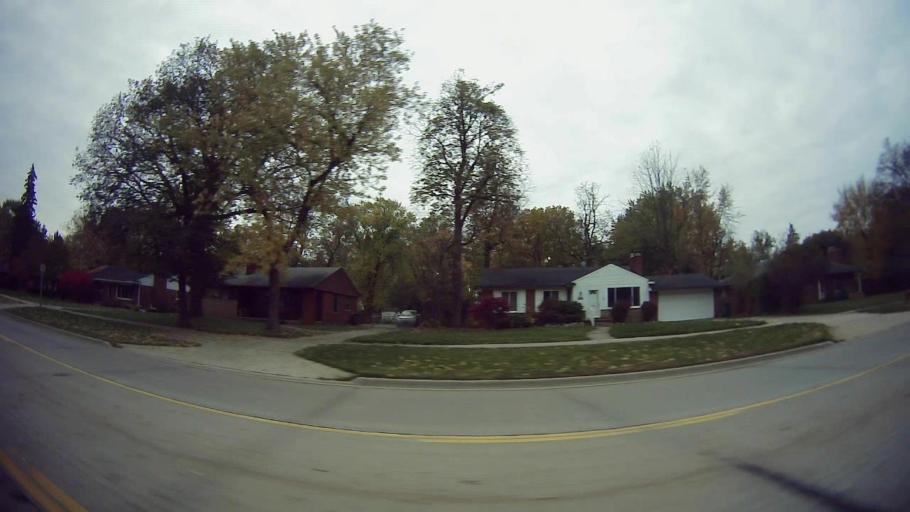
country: US
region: Michigan
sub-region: Oakland County
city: Beverly Hills
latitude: 42.5316
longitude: -83.2197
